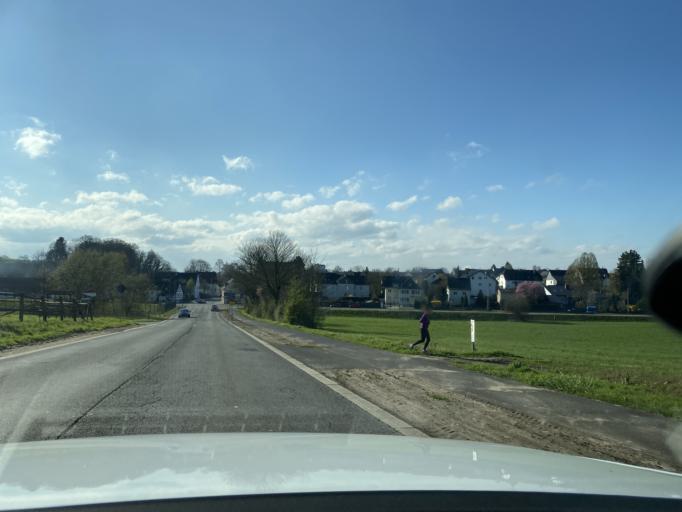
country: DE
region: North Rhine-Westphalia
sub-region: Regierungsbezirk Koln
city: Bergisch Gladbach
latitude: 51.0061
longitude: 7.1294
